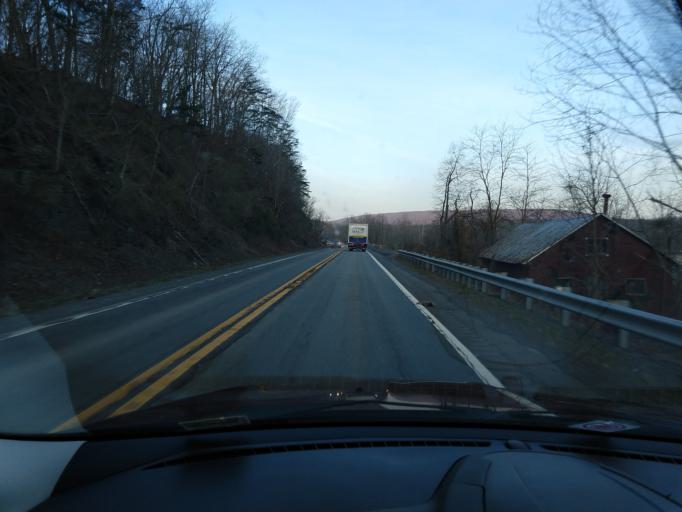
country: US
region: Virginia
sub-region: Frederick County
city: Shawnee Land
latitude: 39.4028
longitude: -78.4187
